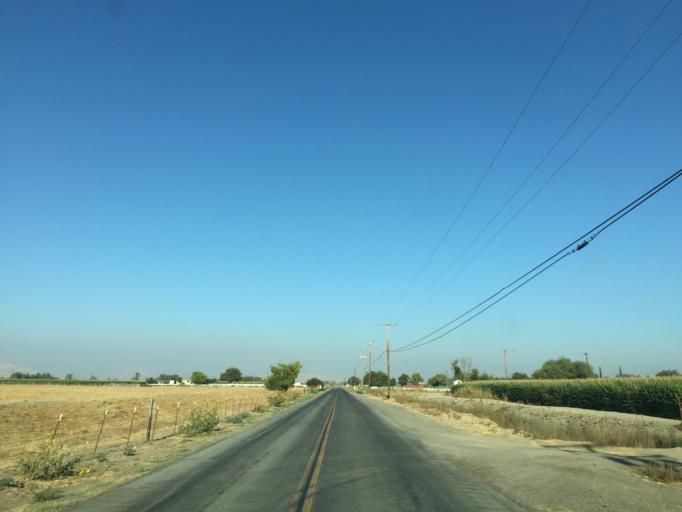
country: US
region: California
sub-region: Tulare County
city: London
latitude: 36.4436
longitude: -119.3680
